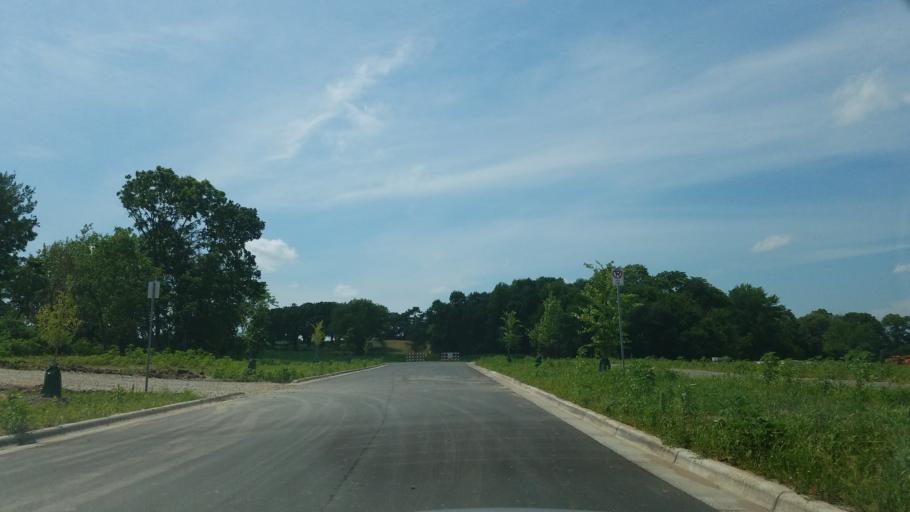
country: US
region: Minnesota
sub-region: Washington County
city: Woodbury
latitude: 44.8872
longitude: -92.9531
